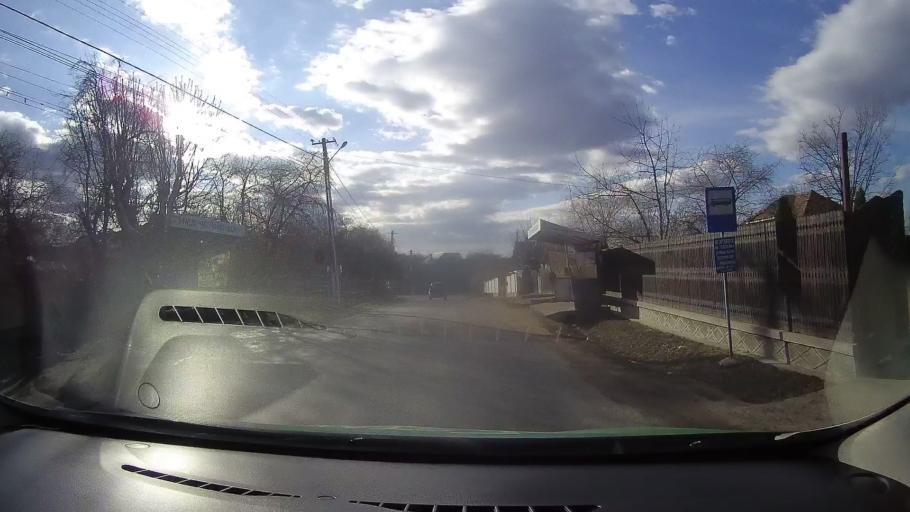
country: RO
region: Dambovita
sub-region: Comuna Ulmi
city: Ulmi
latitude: 44.8899
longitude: 25.5069
